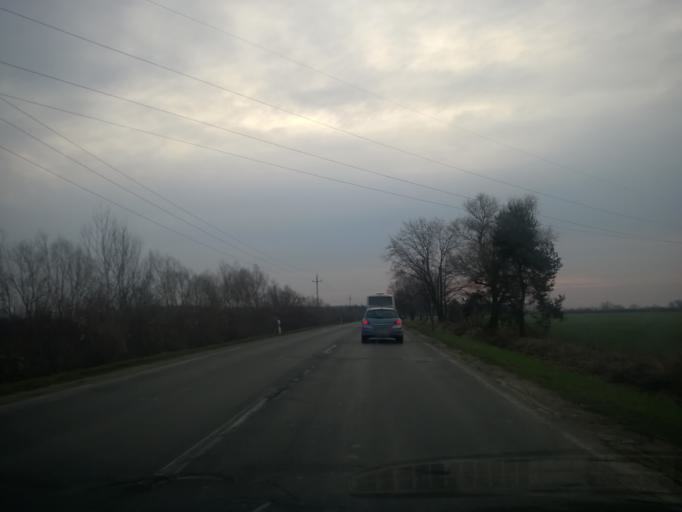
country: HU
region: Baranya
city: Szigetvar
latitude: 46.0492
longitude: 17.8408
